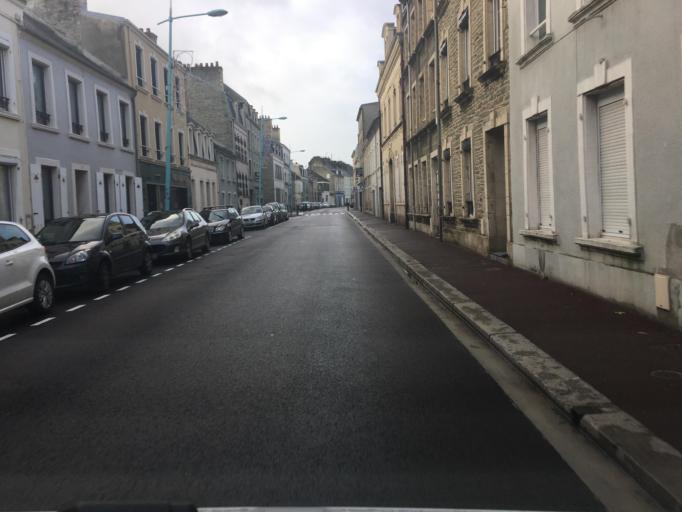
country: FR
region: Lower Normandy
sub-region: Departement de la Manche
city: Cherbourg-Octeville
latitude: 49.6387
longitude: -1.6083
